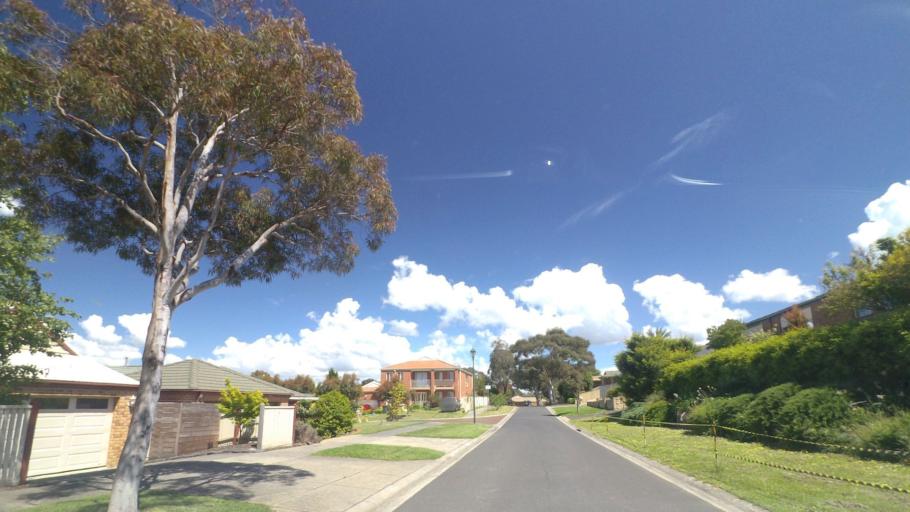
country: AU
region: Victoria
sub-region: Maroondah
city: Croydon South
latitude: -37.8180
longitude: 145.2762
